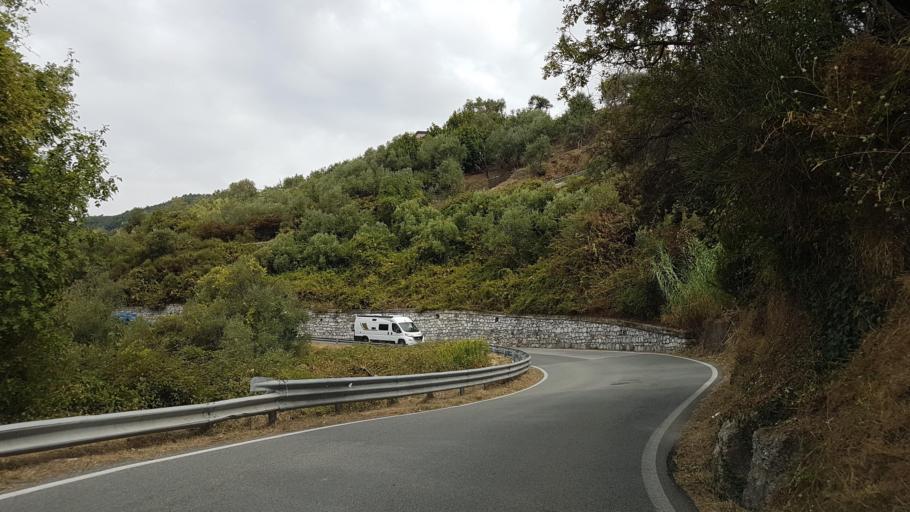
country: IT
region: Liguria
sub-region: Provincia di La Spezia
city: Levanto
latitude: 44.1932
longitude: 9.6284
